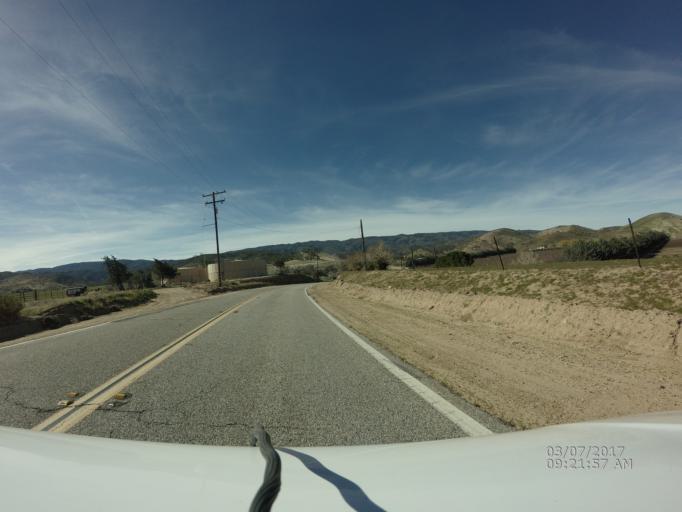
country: US
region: California
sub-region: Los Angeles County
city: Green Valley
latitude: 34.7675
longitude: -118.5903
